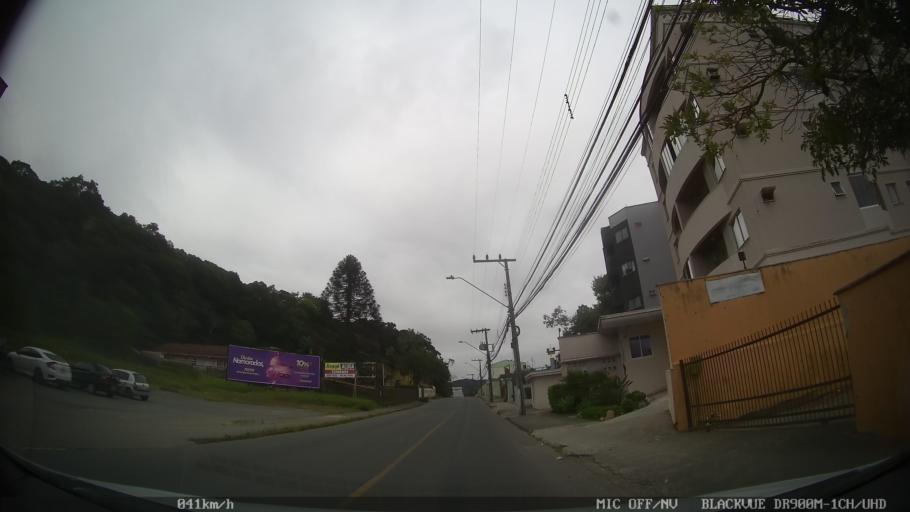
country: BR
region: Santa Catarina
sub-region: Joinville
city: Joinville
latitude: -26.2641
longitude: -48.8537
